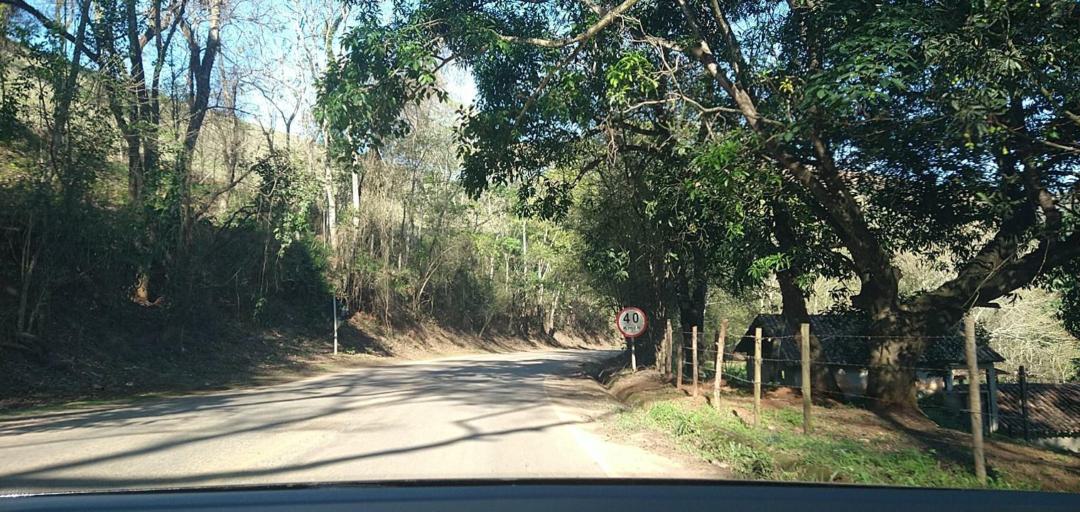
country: BR
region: Minas Gerais
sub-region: Ponte Nova
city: Ponte Nova
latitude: -20.2465
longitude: -42.8888
